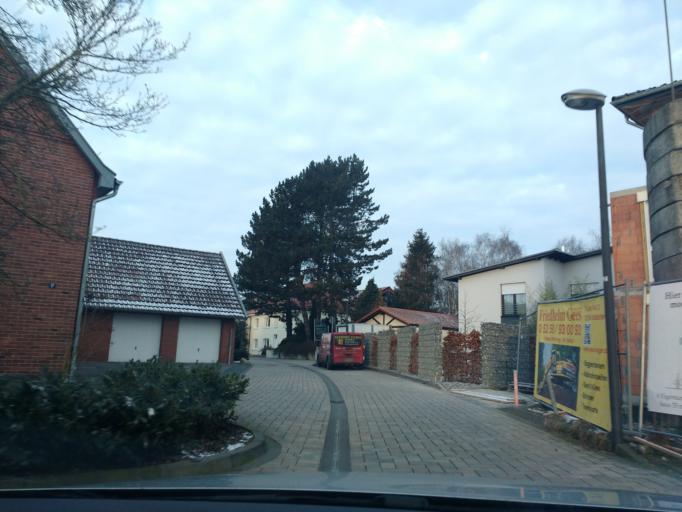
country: DE
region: North Rhine-Westphalia
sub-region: Regierungsbezirk Detmold
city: Paderborn
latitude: 51.7308
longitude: 8.6887
